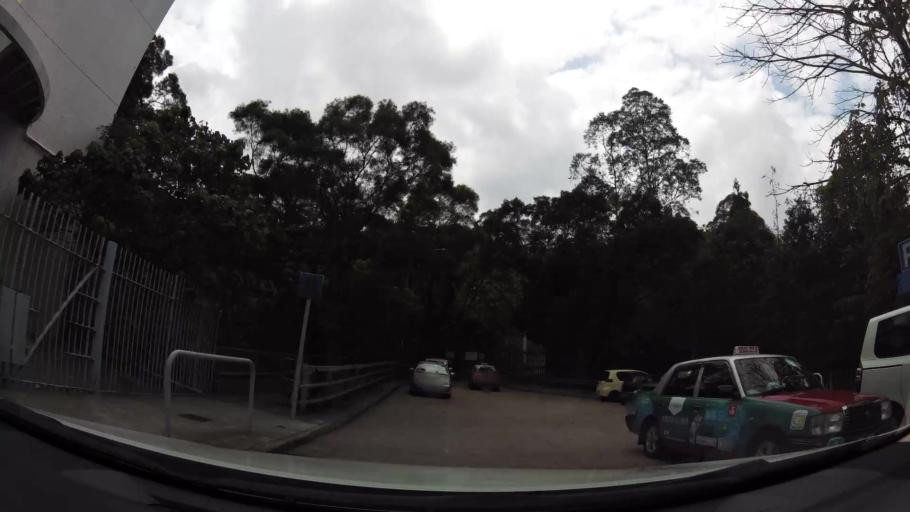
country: HK
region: Wanchai
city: Wan Chai
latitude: 22.2823
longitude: 114.1988
